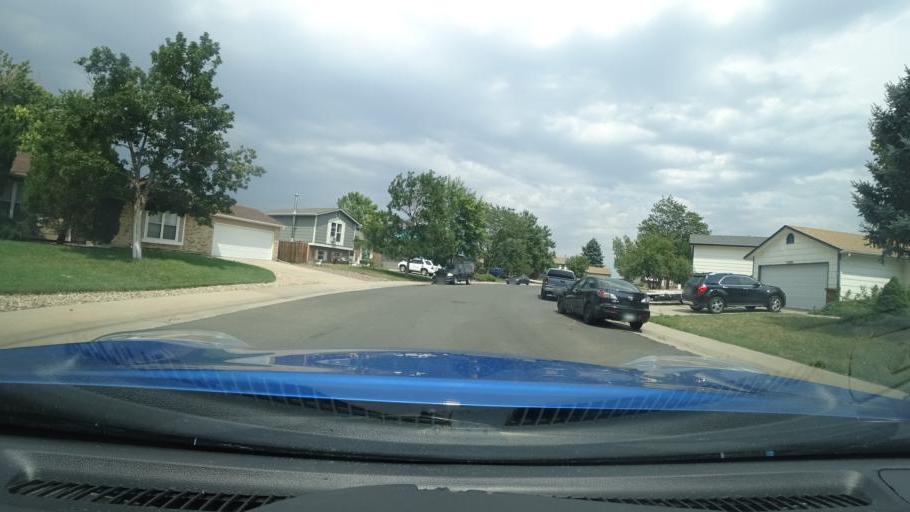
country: US
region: Colorado
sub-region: Adams County
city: Aurora
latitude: 39.6889
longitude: -104.7610
